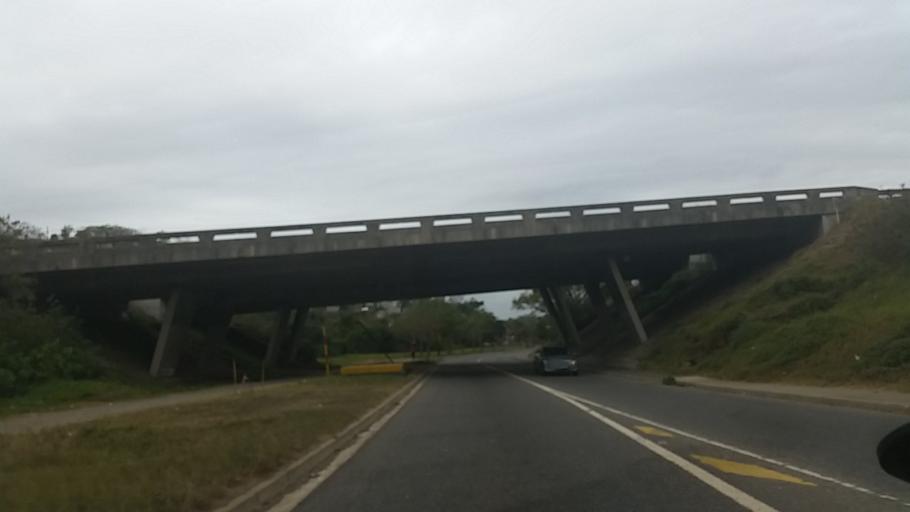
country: ZA
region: KwaZulu-Natal
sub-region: eThekwini Metropolitan Municipality
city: Berea
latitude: -29.8570
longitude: 30.9503
